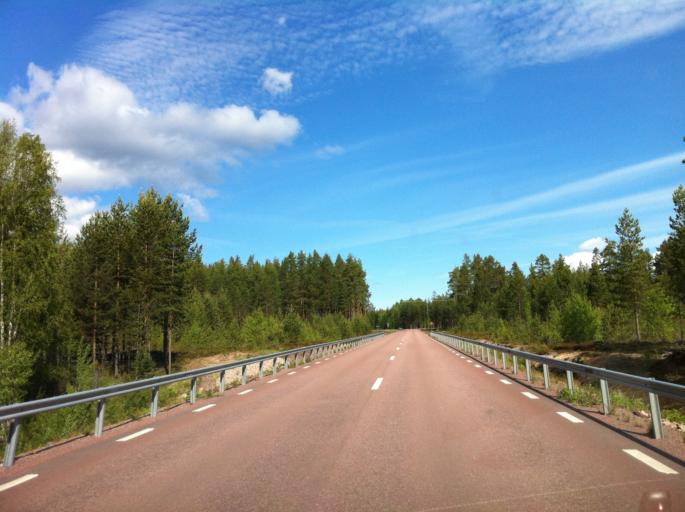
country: SE
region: Dalarna
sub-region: Mora Kommun
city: Mora
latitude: 60.9628
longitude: 14.5219
